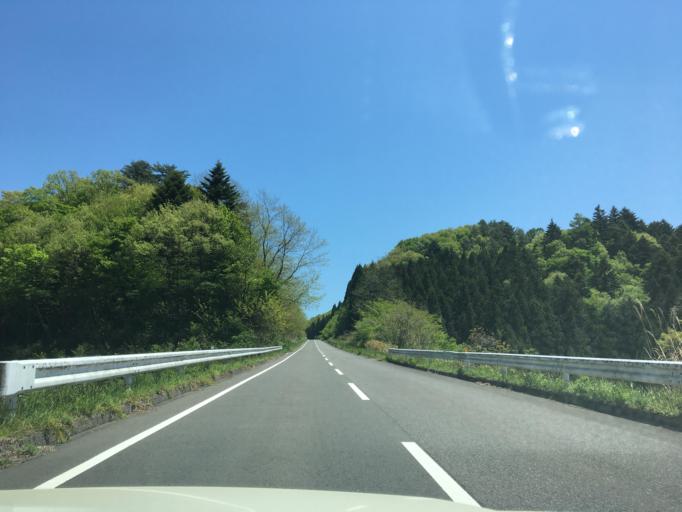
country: JP
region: Fukushima
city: Funehikimachi-funehiki
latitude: 37.3816
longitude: 140.6097
